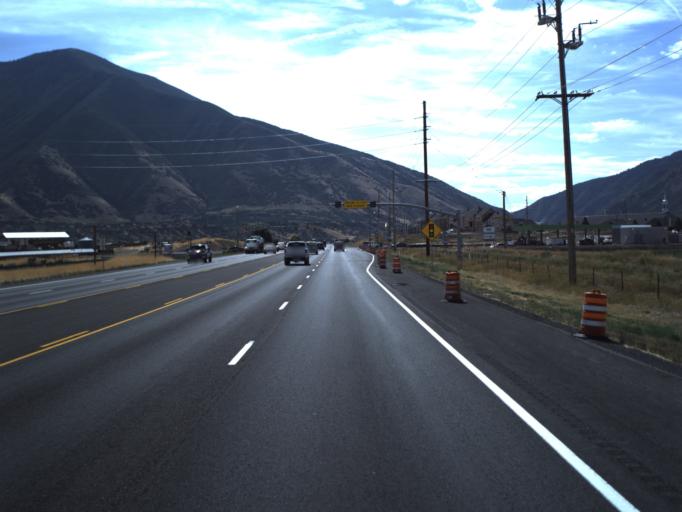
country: US
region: Utah
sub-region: Utah County
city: Spanish Fork
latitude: 40.1006
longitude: -111.6149
